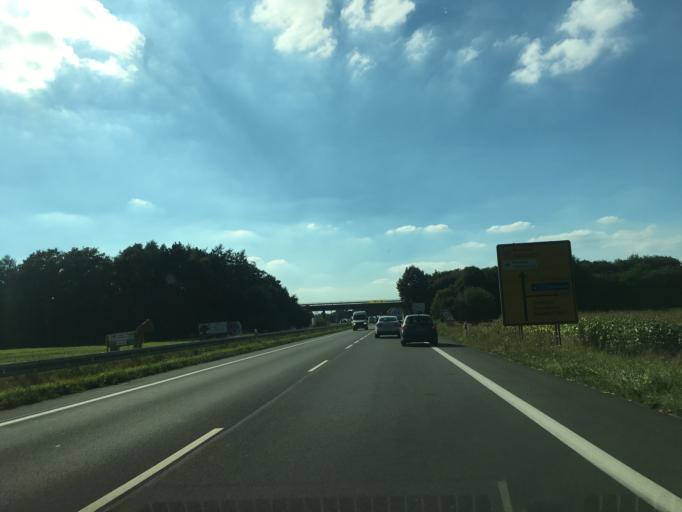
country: DE
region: North Rhine-Westphalia
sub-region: Regierungsbezirk Munster
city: Warendorf
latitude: 51.9488
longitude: 8.0192
